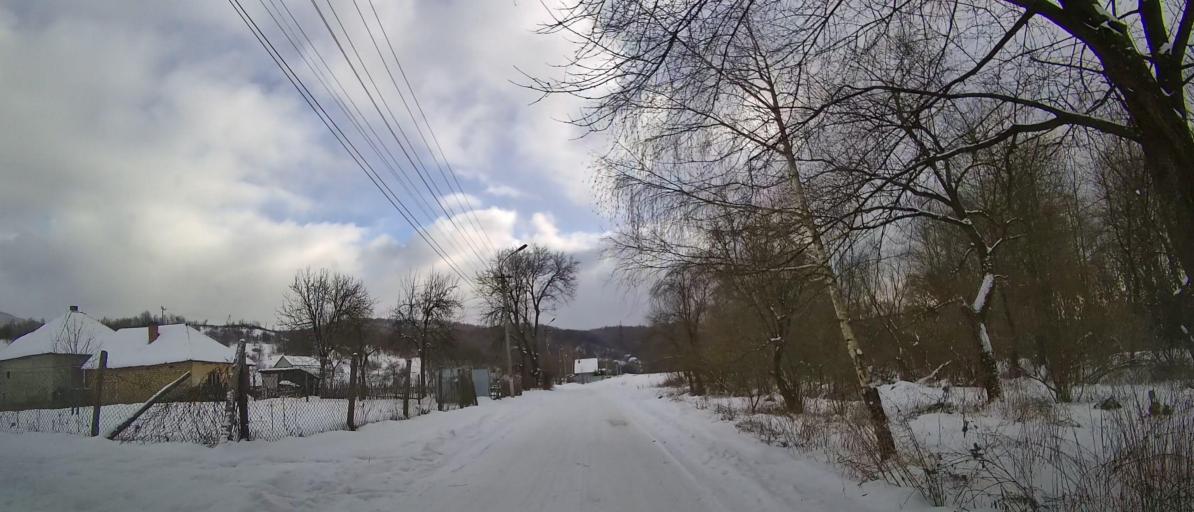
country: UA
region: Zakarpattia
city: Velykyi Bereznyi
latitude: 48.9109
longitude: 22.4658
